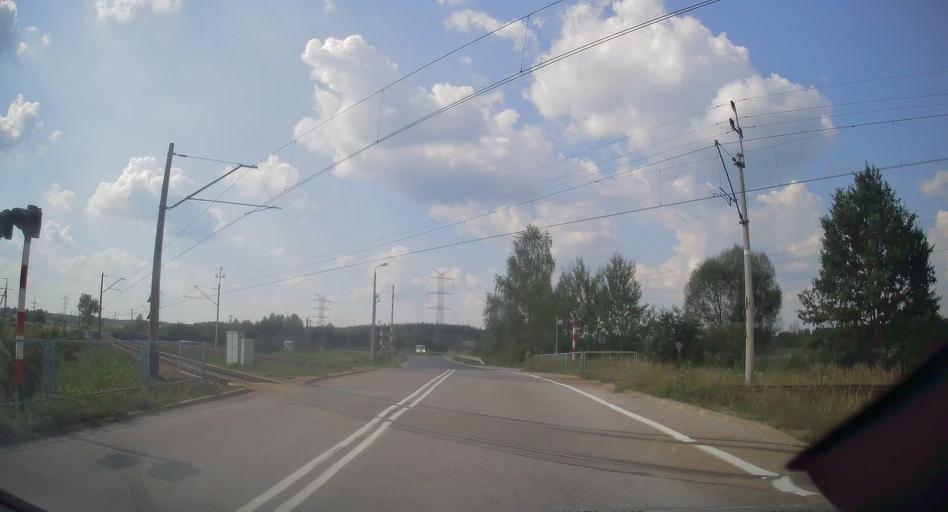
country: PL
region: Swietokrzyskie
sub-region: Powiat jedrzejowski
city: Malogoszcz
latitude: 50.8659
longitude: 20.3229
